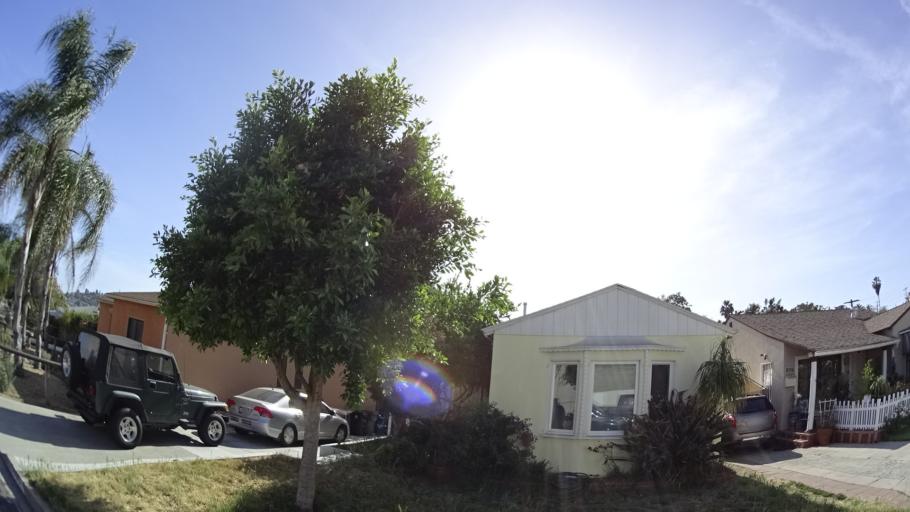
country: US
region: California
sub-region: Los Angeles County
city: Belvedere
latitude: 34.0630
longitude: -118.1761
